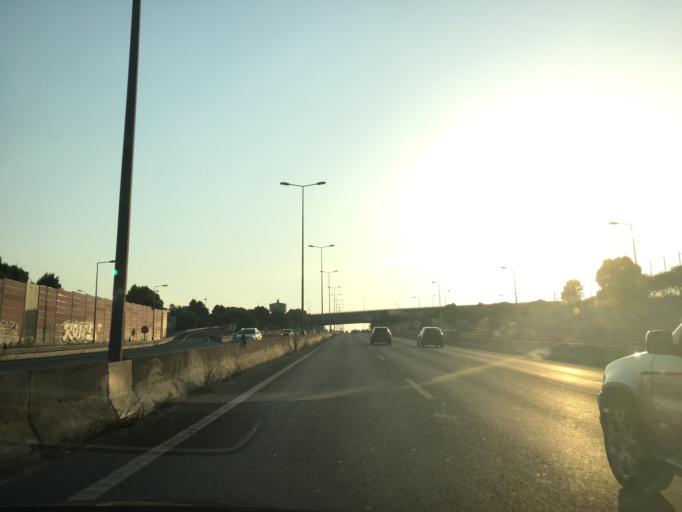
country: PT
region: Lisbon
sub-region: Sintra
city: Queluz
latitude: 38.7478
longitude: -9.2689
